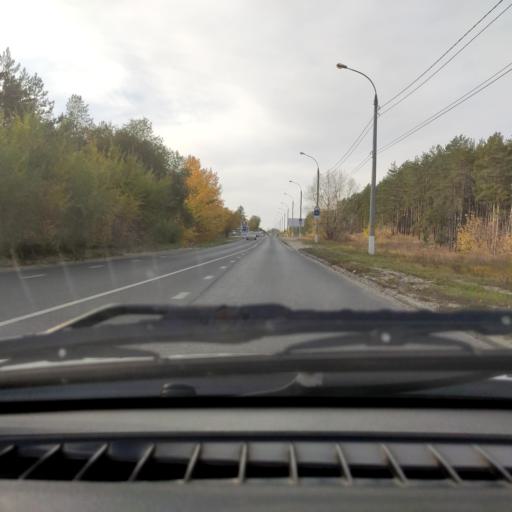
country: RU
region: Samara
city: Zhigulevsk
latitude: 53.4770
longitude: 49.4515
